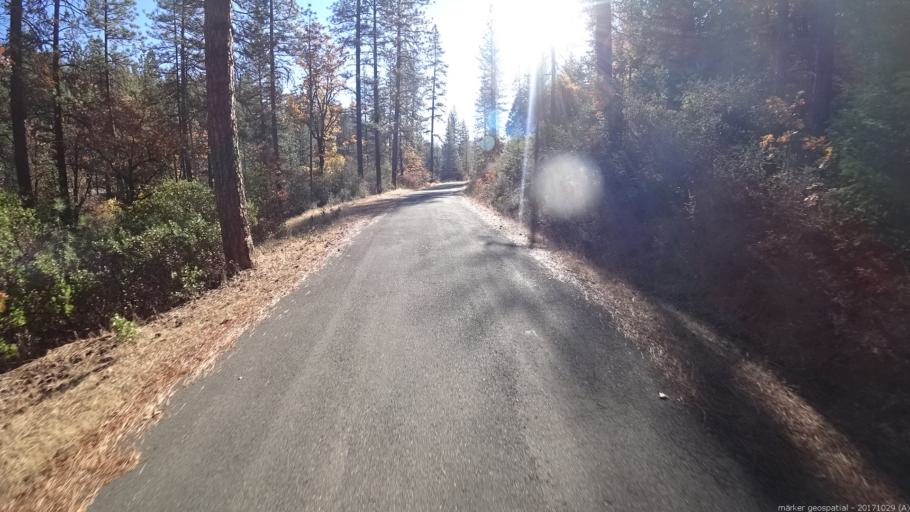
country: US
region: California
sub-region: Trinity County
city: Hayfork
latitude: 40.3658
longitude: -122.9705
